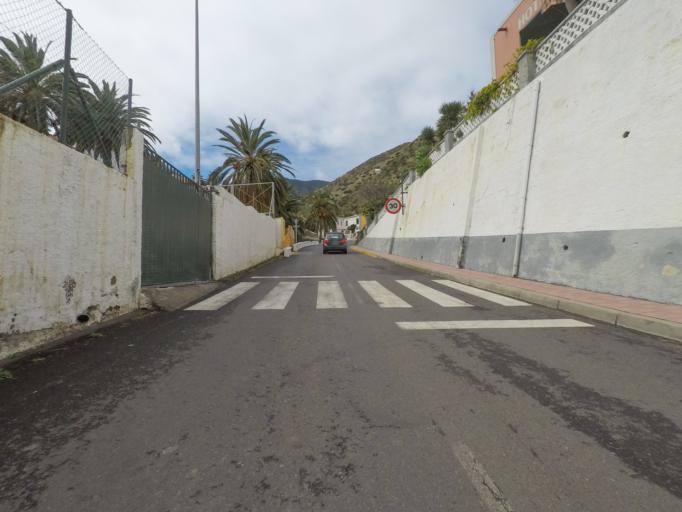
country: ES
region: Canary Islands
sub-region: Provincia de Santa Cruz de Tenerife
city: Vallehermosa
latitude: 28.1818
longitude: -17.2648
